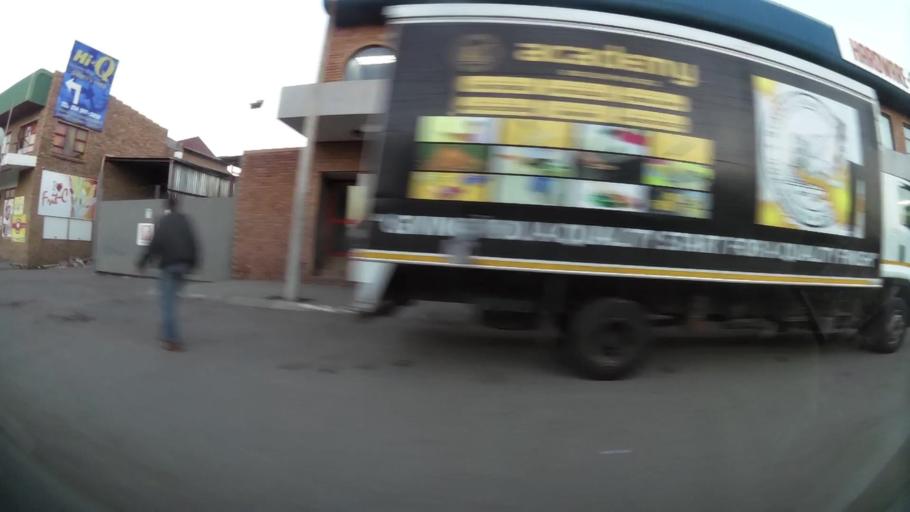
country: ZA
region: North-West
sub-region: Bojanala Platinum District Municipality
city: Rustenburg
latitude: -25.6648
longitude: 27.2404
